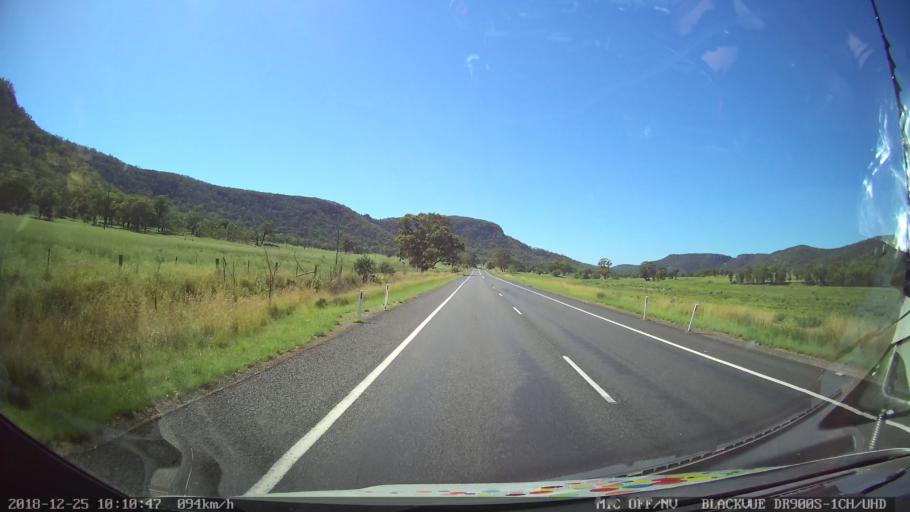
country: AU
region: New South Wales
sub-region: Muswellbrook
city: Denman
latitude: -32.3079
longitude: 150.5251
